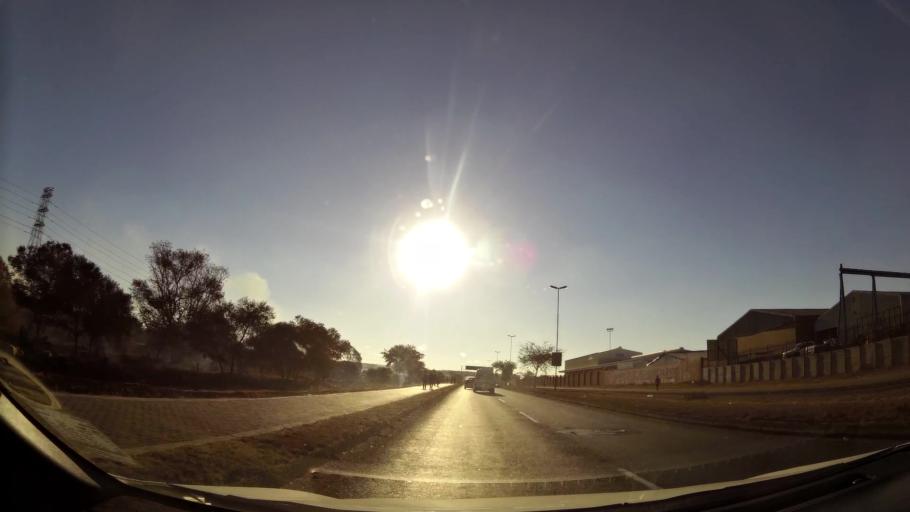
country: ZA
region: Limpopo
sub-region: Capricorn District Municipality
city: Polokwane
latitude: -23.8901
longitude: 29.4330
